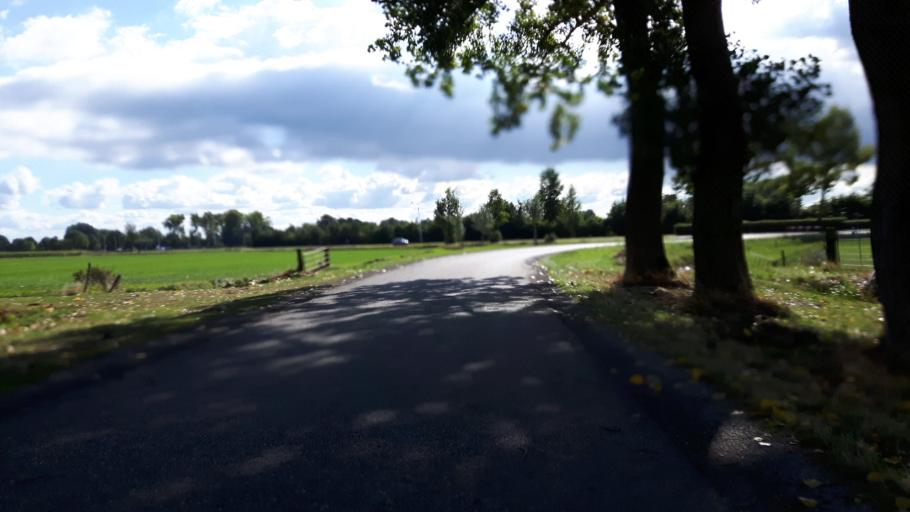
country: NL
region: South Holland
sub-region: Gemeente Leerdam
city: Leerdam
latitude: 51.8874
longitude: 5.1317
